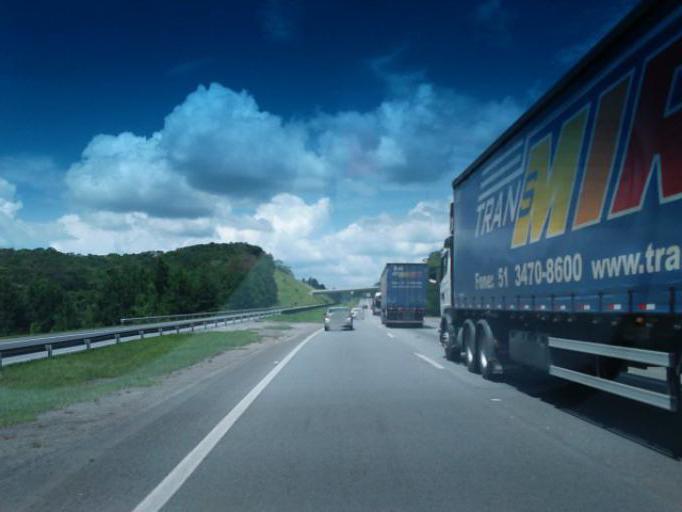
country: BR
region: Sao Paulo
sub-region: Juquitiba
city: Juquitiba
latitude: -23.9547
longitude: -47.1076
